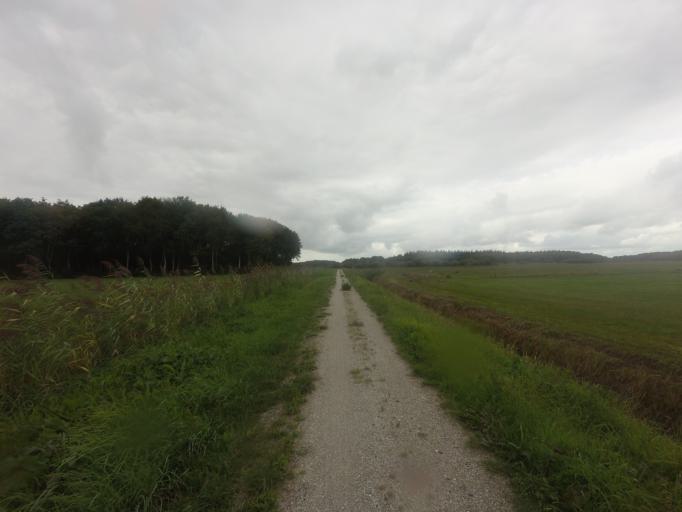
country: NL
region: Friesland
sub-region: Gemeente Weststellingwerf
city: Noordwolde
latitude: 52.9366
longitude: 6.1771
